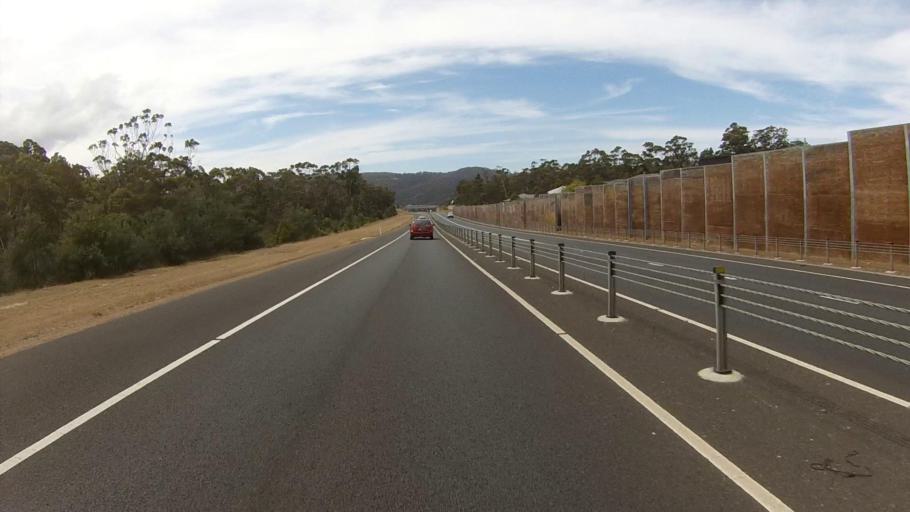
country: AU
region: Tasmania
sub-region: Kingborough
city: Kingston
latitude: -42.9795
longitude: 147.2951
